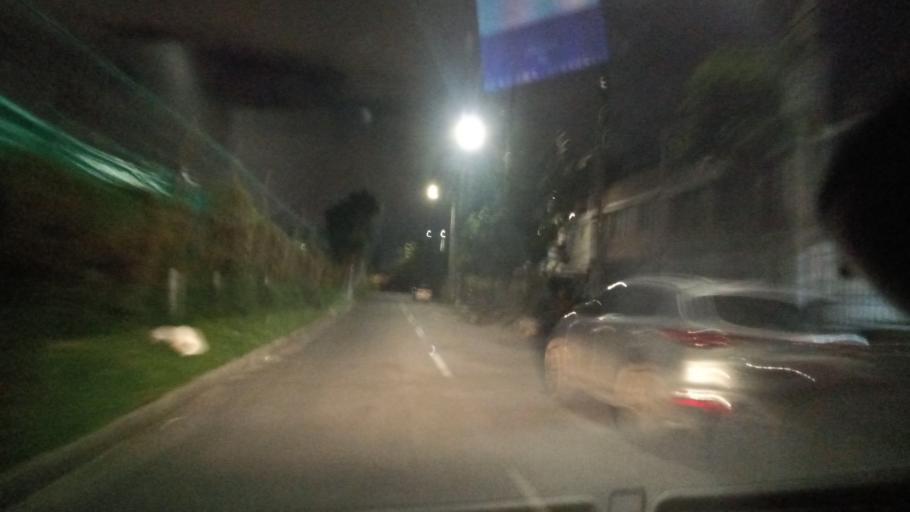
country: CO
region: Cundinamarca
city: Funza
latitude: 4.6677
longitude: -74.1431
